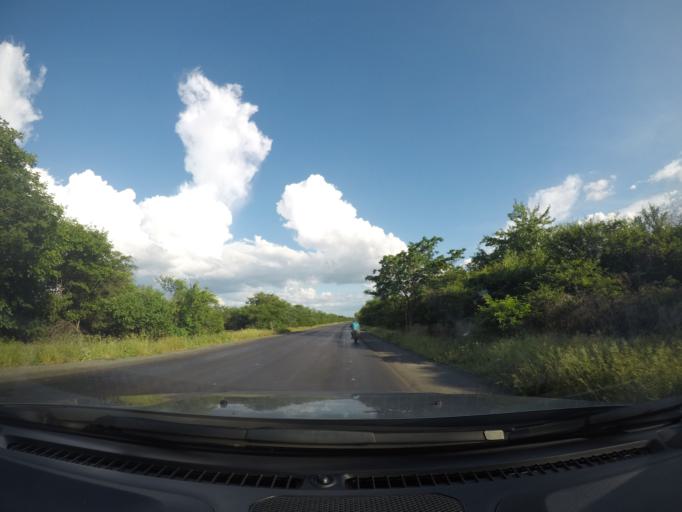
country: BR
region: Bahia
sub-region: Oliveira Dos Brejinhos
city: Oliveira dos Brejinhos
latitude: -12.0906
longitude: -42.9304
